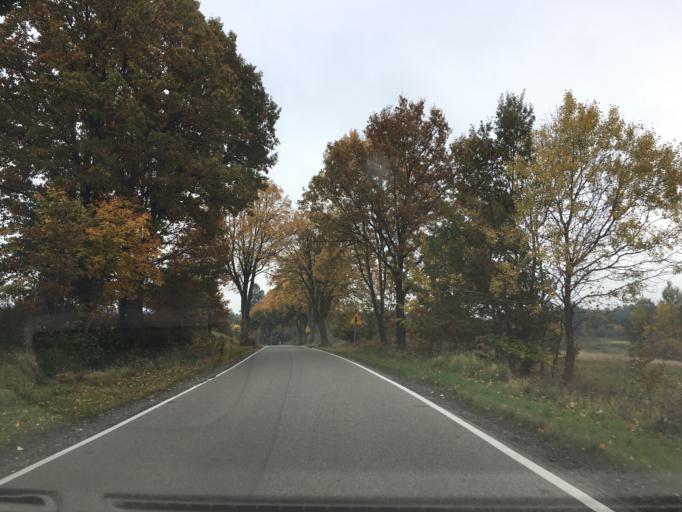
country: PL
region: Pomeranian Voivodeship
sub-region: Powiat wejherowski
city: Luzino
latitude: 54.4686
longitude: 18.0936
